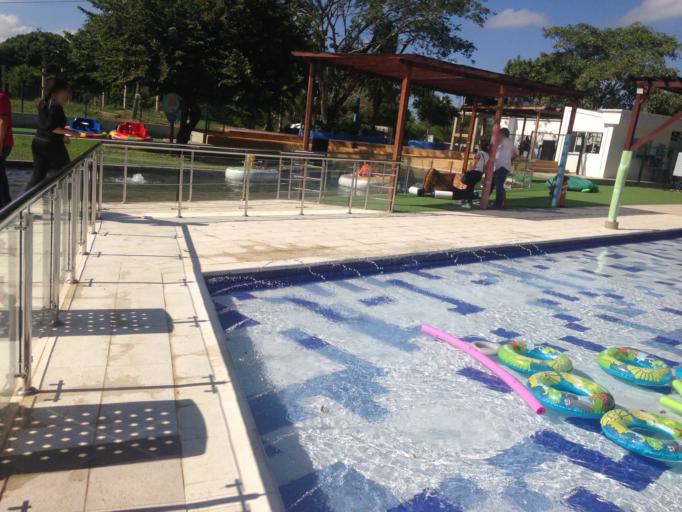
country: CO
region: Atlantico
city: Baranoa
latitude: 10.8413
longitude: -74.9031
